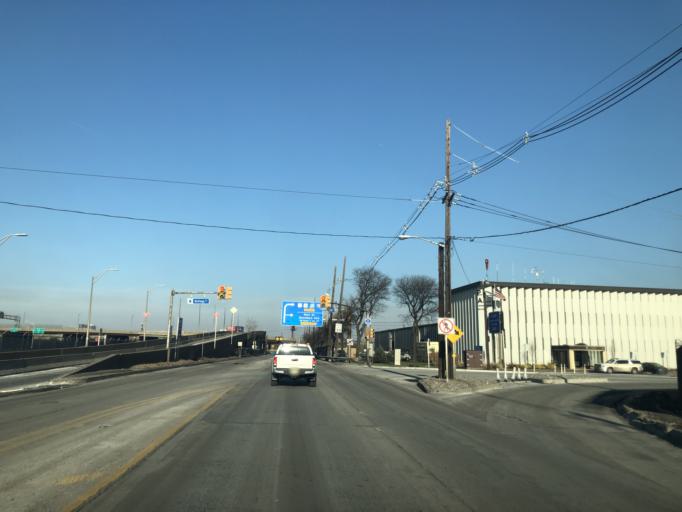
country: US
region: New Jersey
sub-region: Essex County
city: Newark
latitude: 40.7019
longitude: -74.1521
